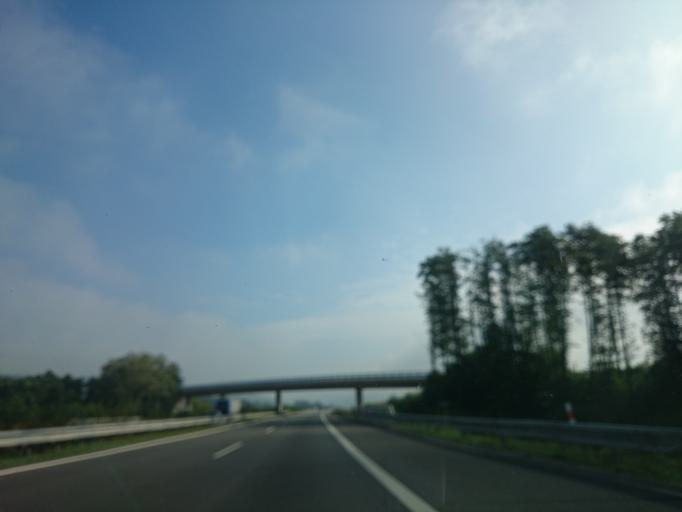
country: CZ
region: Olomoucky
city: Belotin
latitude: 49.6140
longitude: 17.8075
